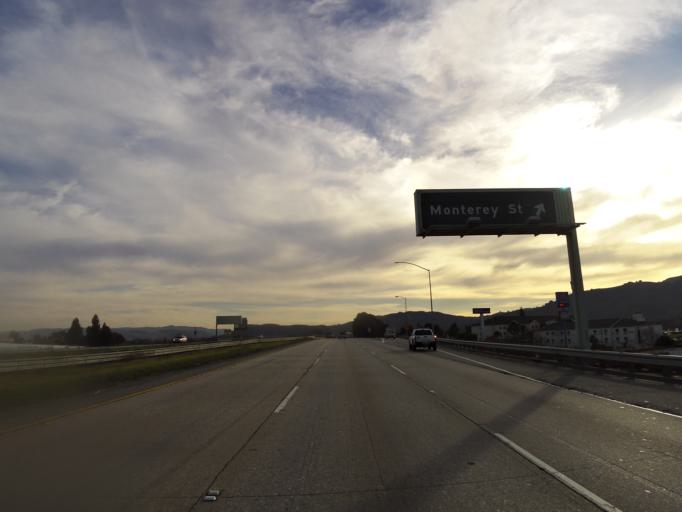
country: US
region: California
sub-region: Santa Clara County
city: Gilroy
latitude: 36.9910
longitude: -121.5578
